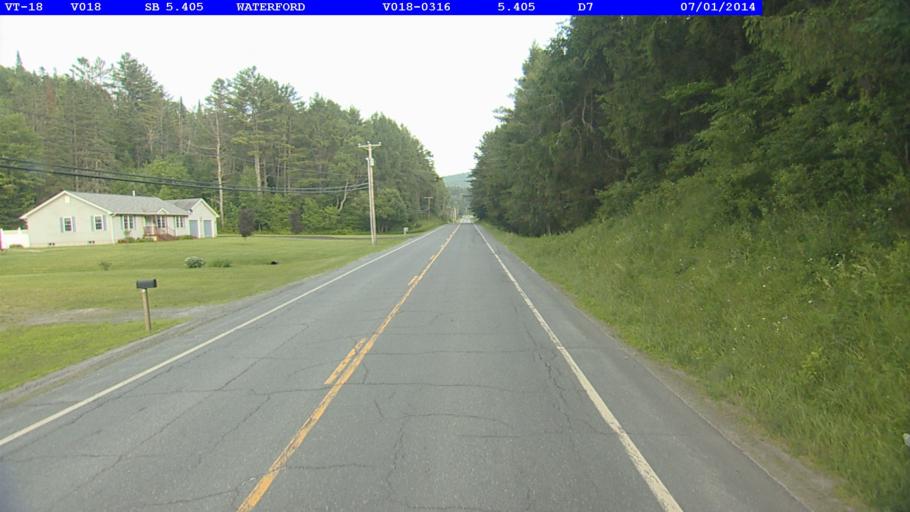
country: US
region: Vermont
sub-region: Caledonia County
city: Saint Johnsbury
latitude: 44.4081
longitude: -71.9288
